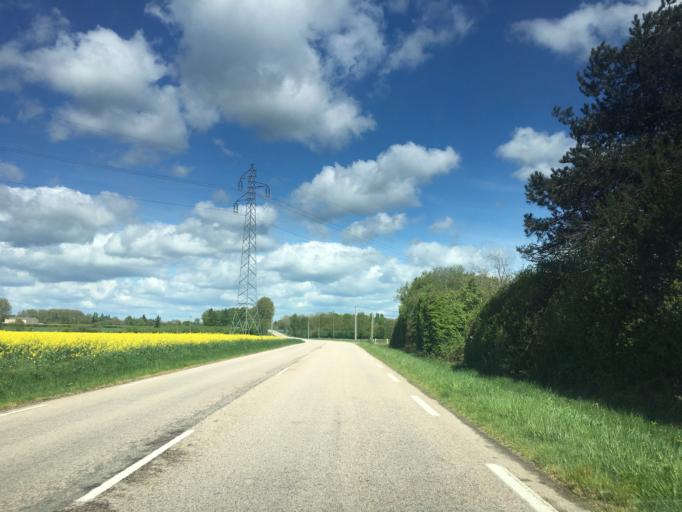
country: FR
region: Lower Normandy
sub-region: Departement de l'Orne
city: Rai
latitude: 48.8120
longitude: 0.5781
